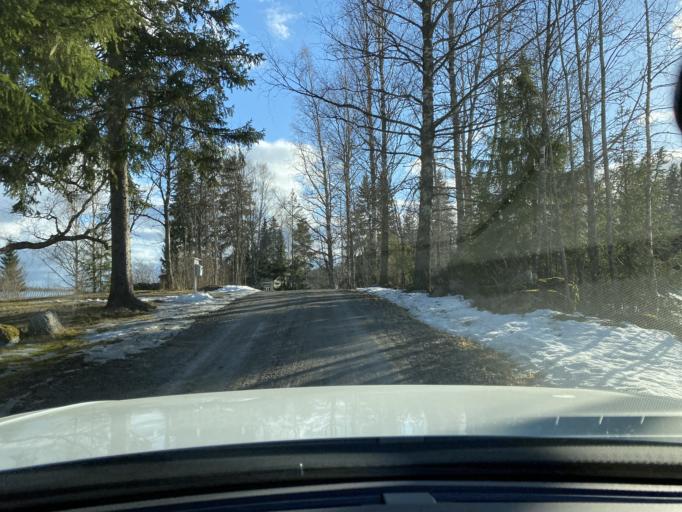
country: FI
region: Pirkanmaa
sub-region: Lounais-Pirkanmaa
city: Mouhijaervi
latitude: 61.4596
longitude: 22.9591
